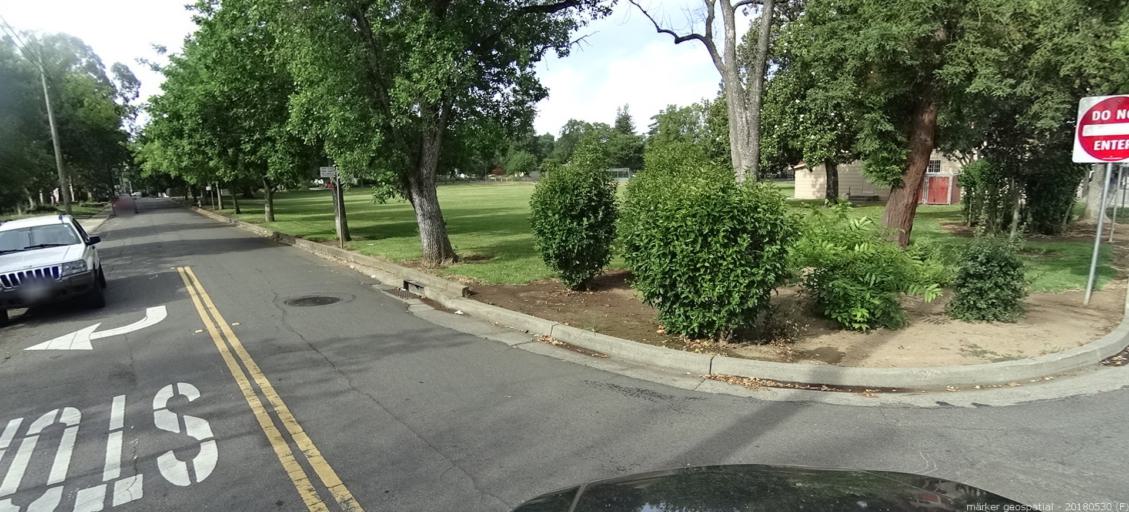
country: US
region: California
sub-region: Sacramento County
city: Sacramento
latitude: 38.6061
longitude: -121.4543
